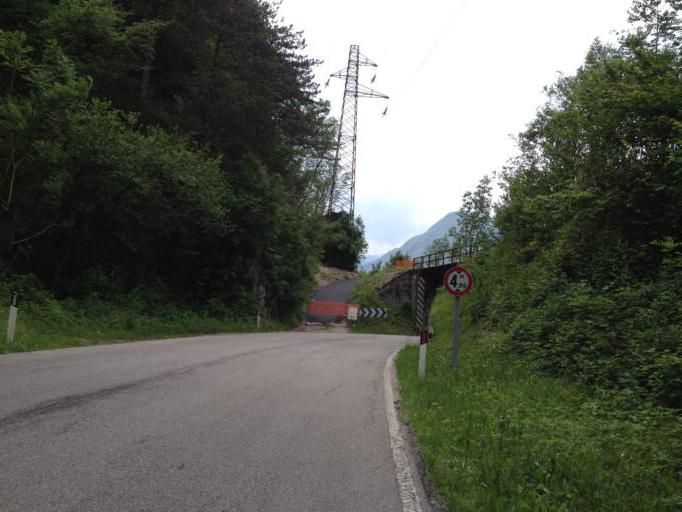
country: IT
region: Friuli Venezia Giulia
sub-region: Provincia di Udine
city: Resiutta
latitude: 46.3949
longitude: 13.2099
